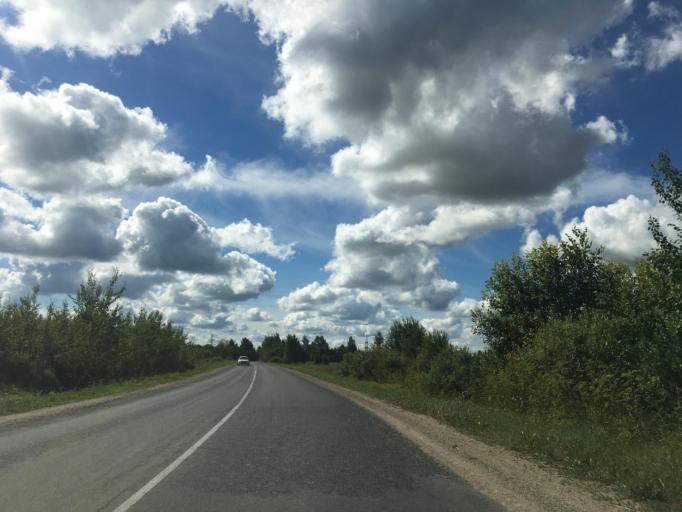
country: RU
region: Pskov
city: Pskov
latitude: 57.7703
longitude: 28.1603
